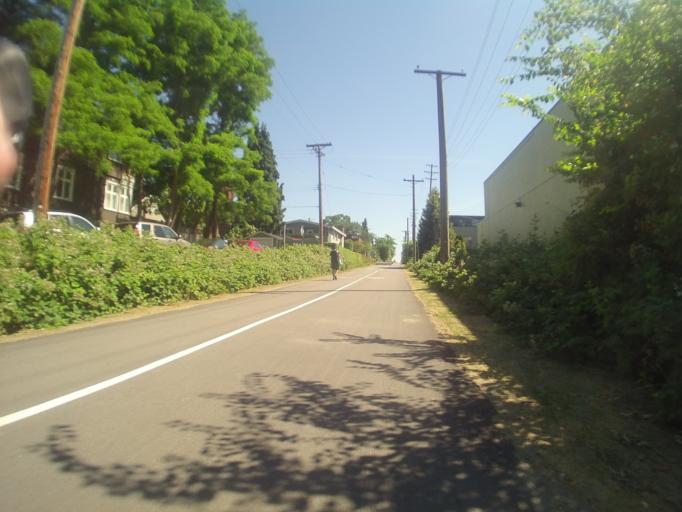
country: CA
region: British Columbia
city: West End
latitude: 49.2600
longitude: -123.1526
